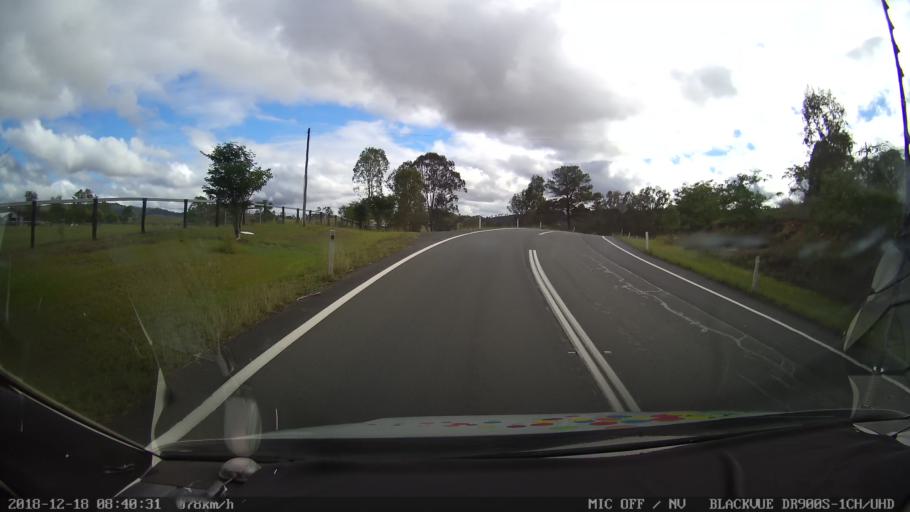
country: AU
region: Queensland
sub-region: Logan
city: Cedar Vale
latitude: -28.2416
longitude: 152.8478
